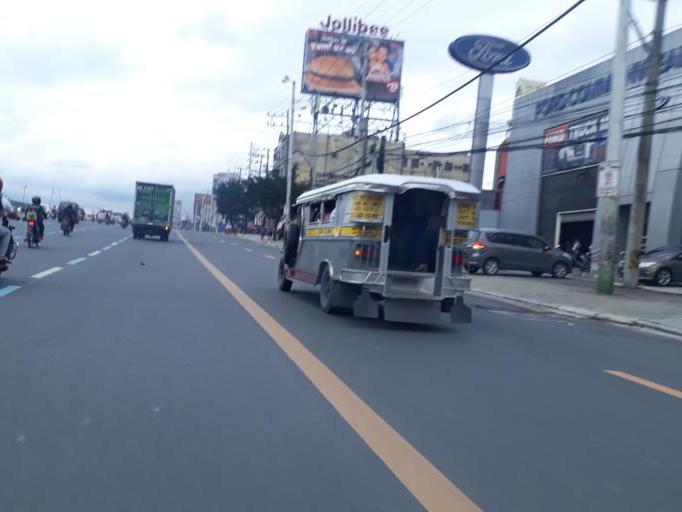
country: PH
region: Metro Manila
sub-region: Quezon City
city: Quezon City
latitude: 14.6664
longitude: 121.0726
